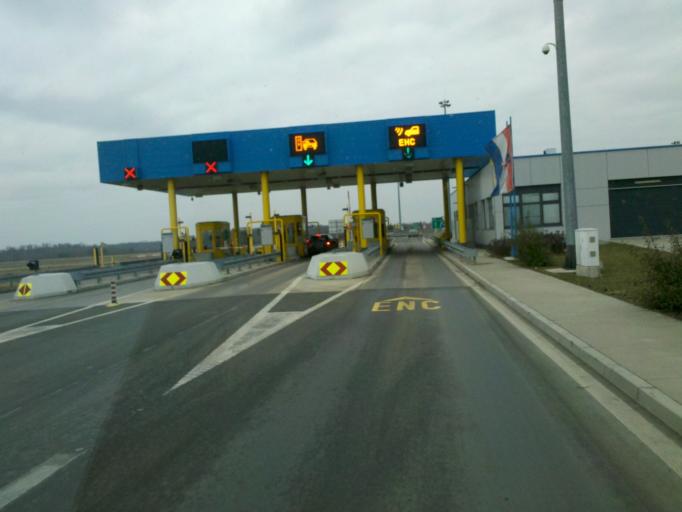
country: HR
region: Grad Zagreb
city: Horvati
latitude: 45.6753
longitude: 15.7572
